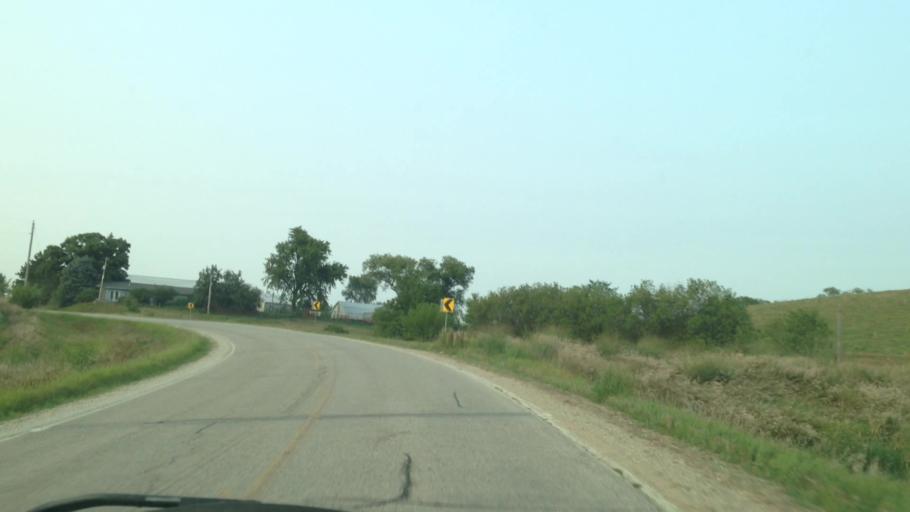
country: US
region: Iowa
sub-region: Iowa County
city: Marengo
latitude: 41.8637
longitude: -92.0892
